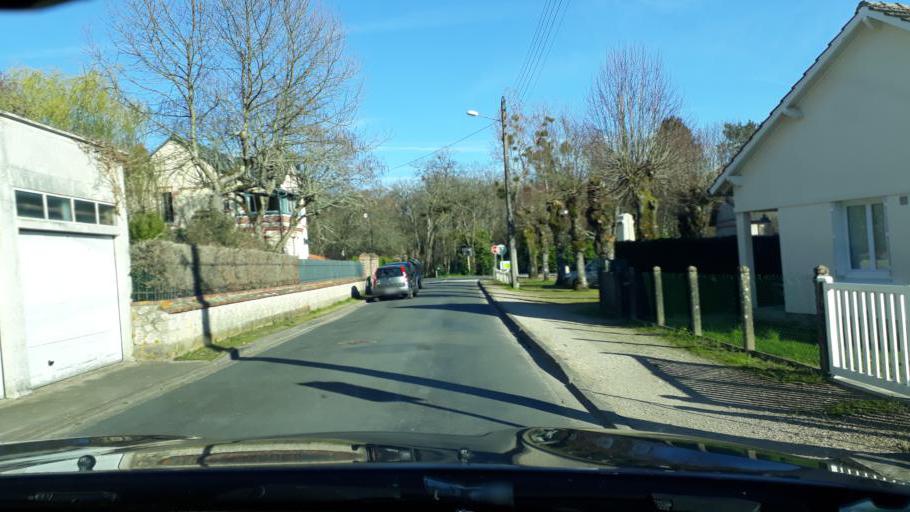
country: FR
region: Centre
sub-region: Departement du Loiret
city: Ligny-le-Ribault
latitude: 47.6863
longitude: 1.7825
